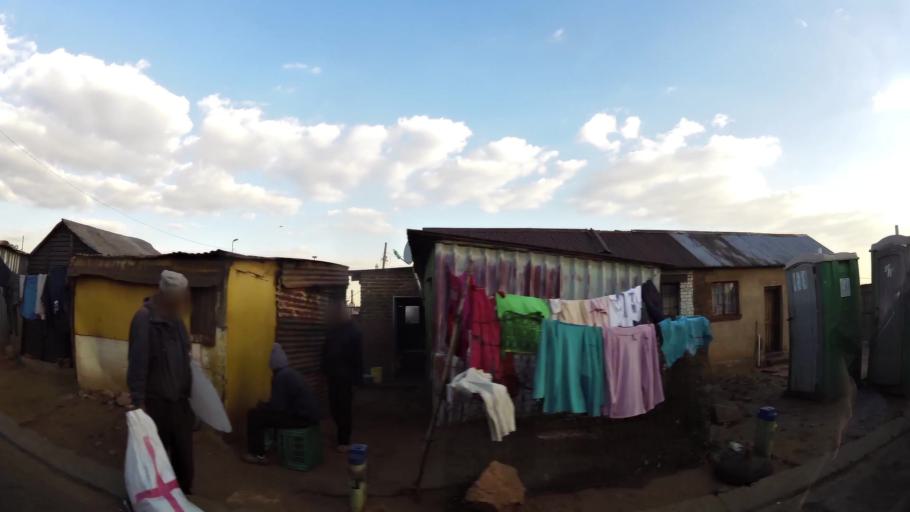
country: ZA
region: Gauteng
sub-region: West Rand District Municipality
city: Krugersdorp
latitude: -26.0788
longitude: 27.7586
